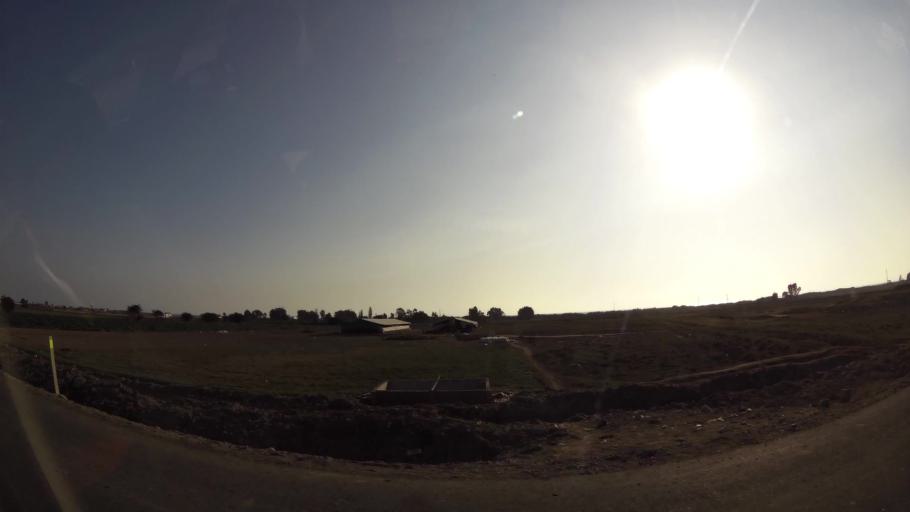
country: PE
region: Ica
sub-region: Provincia de Chincha
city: Chincha Baja
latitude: -13.5551
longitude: -76.1808
